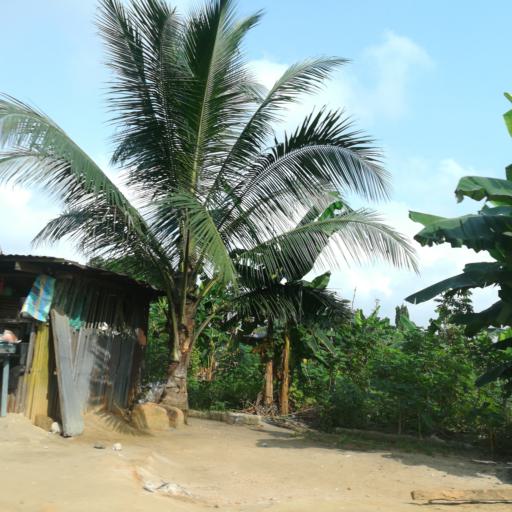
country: NG
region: Rivers
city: Okrika
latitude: 4.7788
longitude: 7.1346
